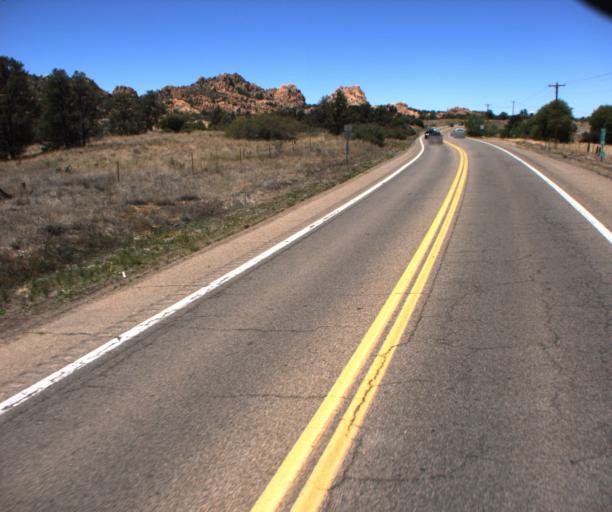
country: US
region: Arizona
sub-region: Yavapai County
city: Prescott
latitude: 34.6163
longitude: -112.4207
